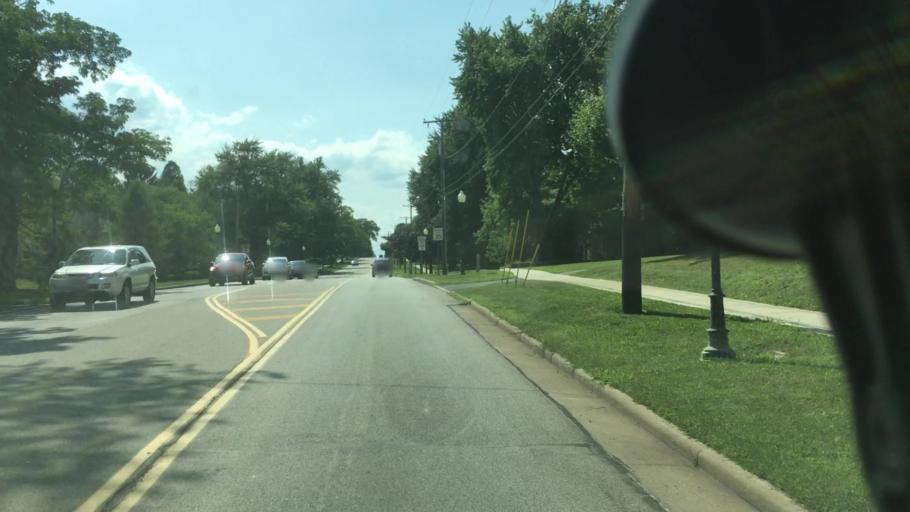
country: US
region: Ohio
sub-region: Mahoning County
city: Canfield
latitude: 41.0248
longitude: -80.7501
